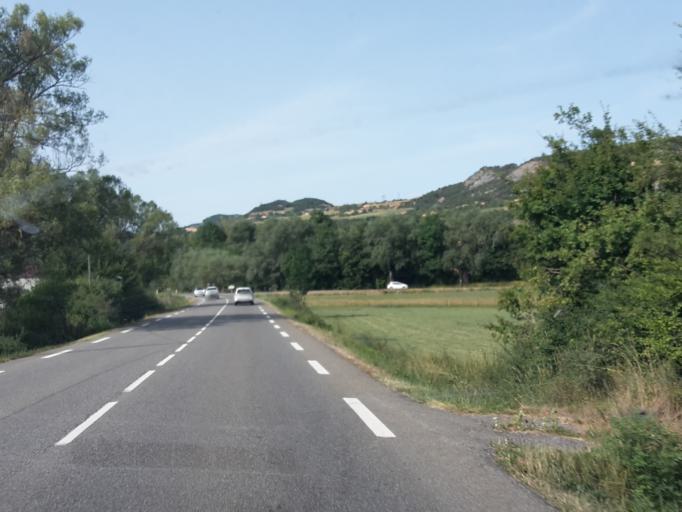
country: FR
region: Provence-Alpes-Cote d'Azur
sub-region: Departement des Hautes-Alpes
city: La Batie-Neuve
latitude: 44.5512
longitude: 6.2039
